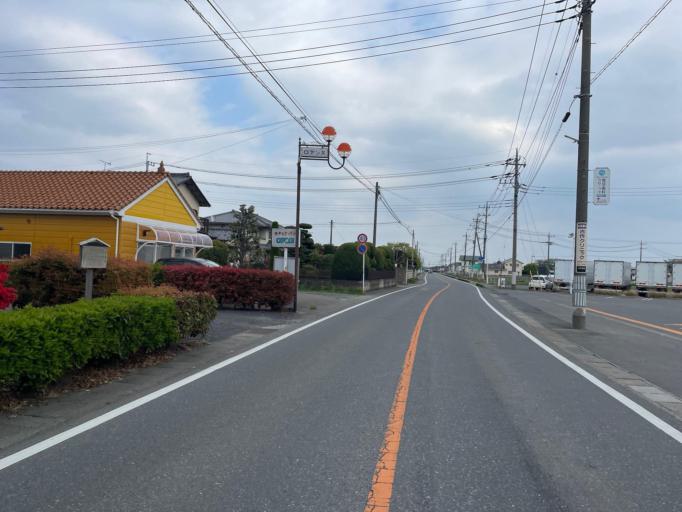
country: JP
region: Gunma
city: Isesaki
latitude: 36.2815
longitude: 139.2021
